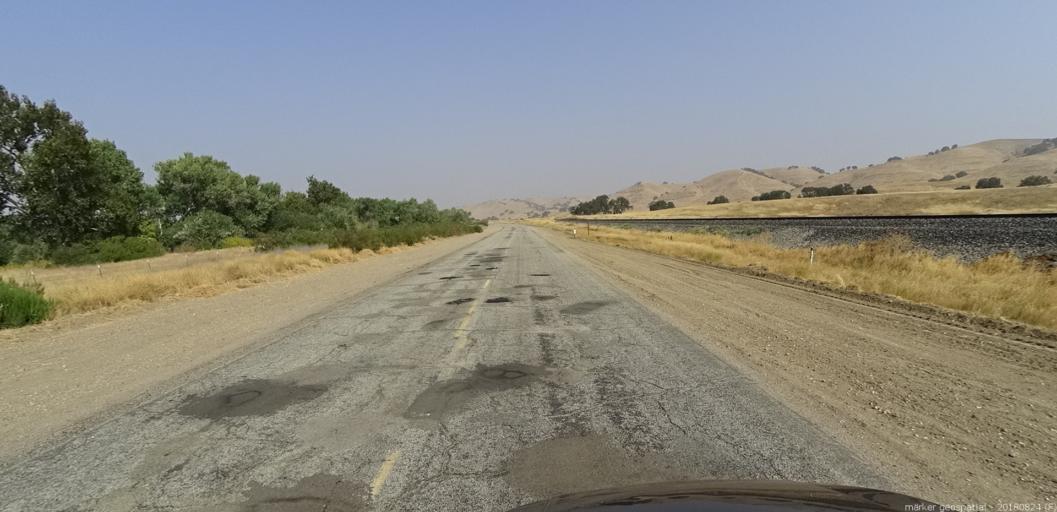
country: US
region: California
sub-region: San Luis Obispo County
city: San Miguel
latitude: 35.8497
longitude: -120.7554
